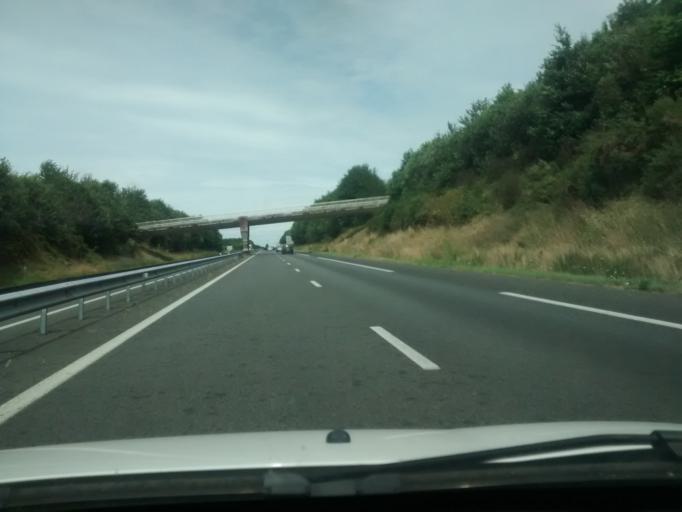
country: FR
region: Brittany
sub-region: Departement d'Ille-et-Vilaine
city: Saint-Etienne-en-Cogles
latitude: 48.4483
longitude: -1.3254
